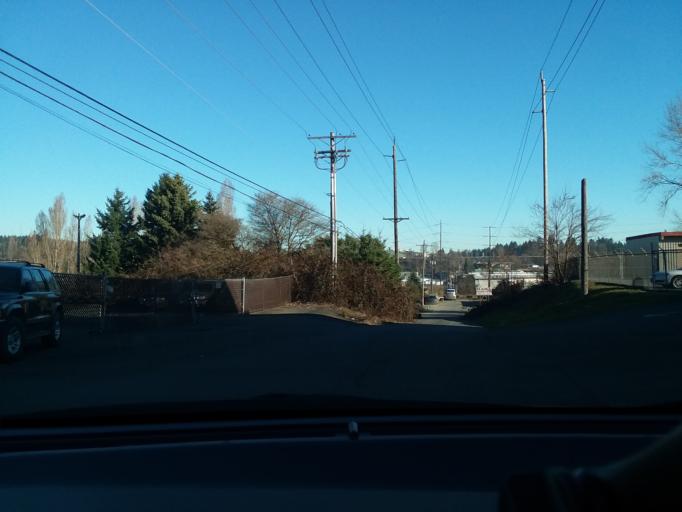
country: US
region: Washington
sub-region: Pierce County
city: Tacoma
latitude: 47.2265
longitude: -122.4764
